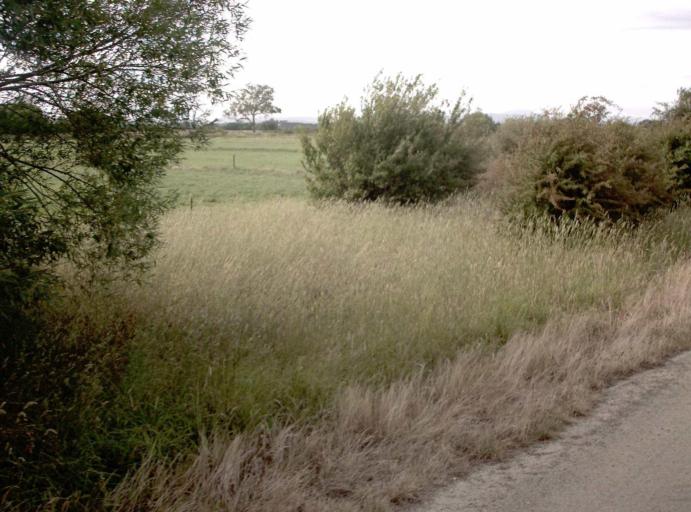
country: AU
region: Victoria
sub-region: Wellington
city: Heyfield
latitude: -37.9781
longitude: 146.8887
